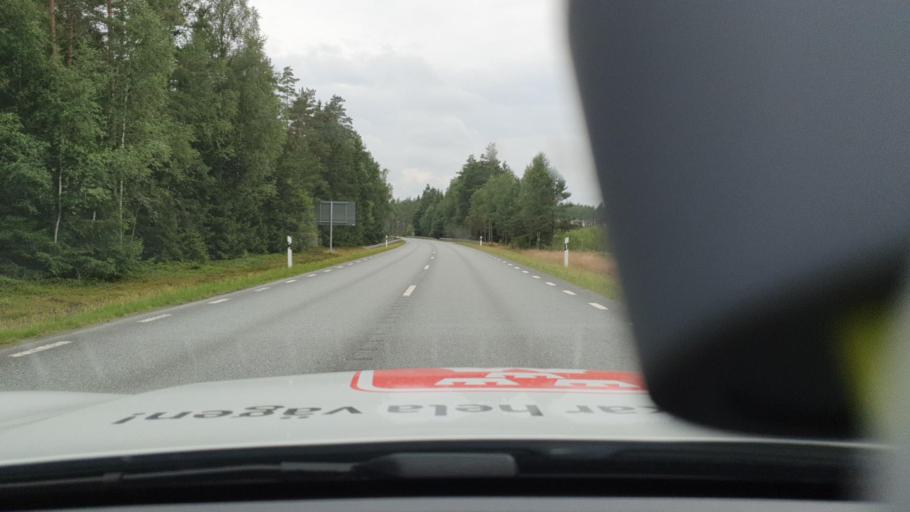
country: SE
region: Joenkoeping
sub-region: Gislaveds Kommun
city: Gislaved
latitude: 57.4207
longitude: 13.6041
